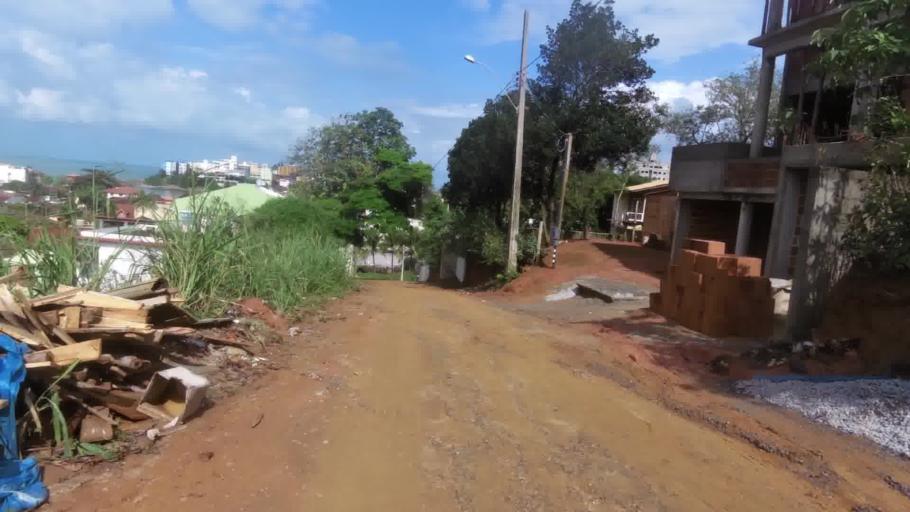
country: BR
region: Espirito Santo
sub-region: Piuma
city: Piuma
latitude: -20.8275
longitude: -40.6911
